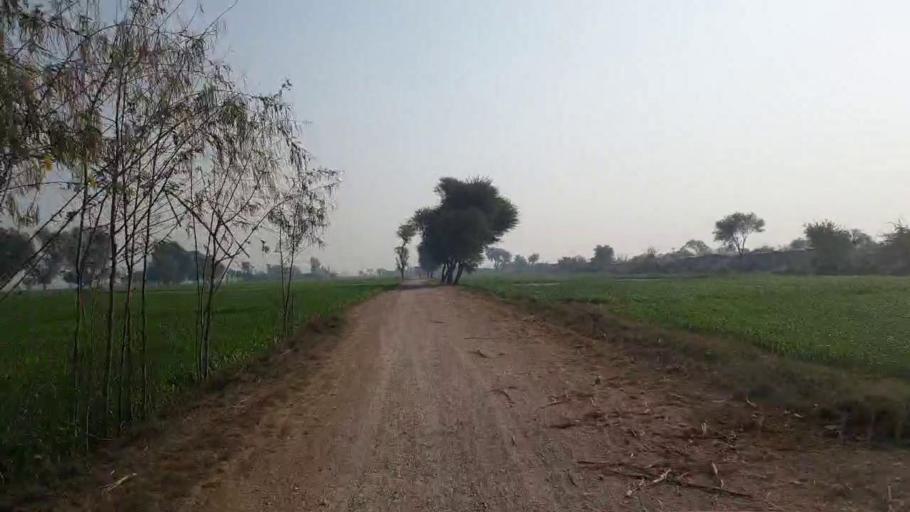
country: PK
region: Sindh
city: Sakrand
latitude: 26.0005
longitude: 68.3647
